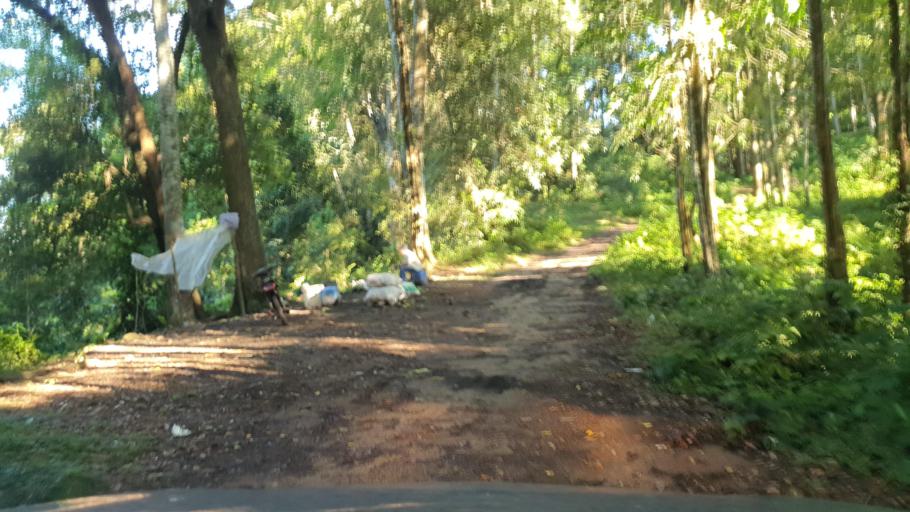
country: TH
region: Chiang Mai
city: Mae On
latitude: 18.8105
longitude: 99.3568
